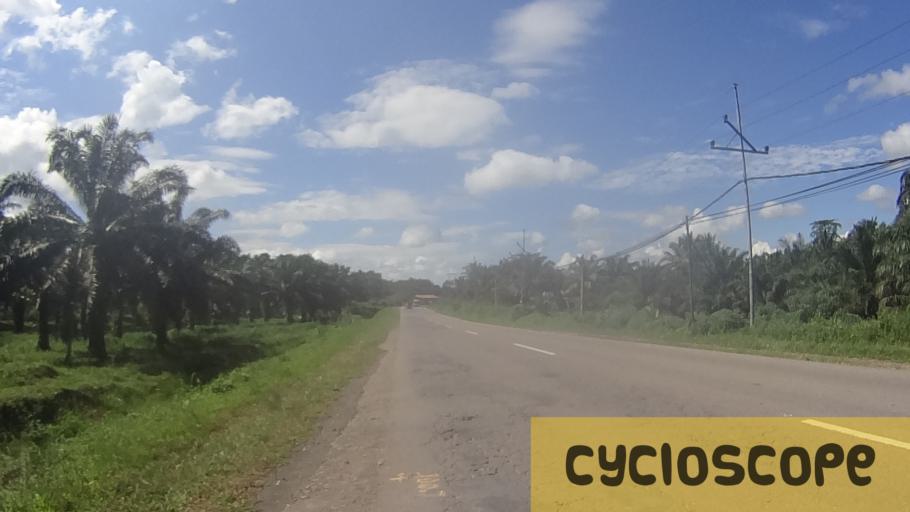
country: MY
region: Sabah
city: Beaufort
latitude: 5.3179
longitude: 115.7101
